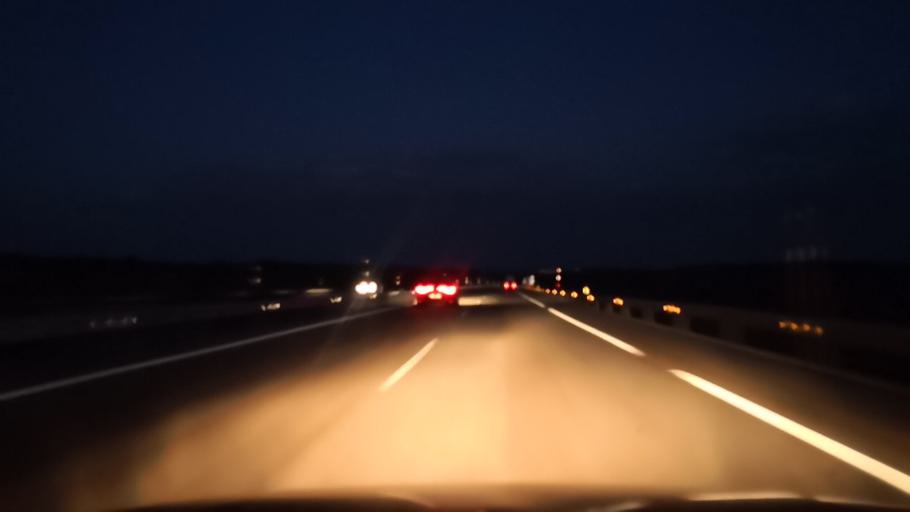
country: ES
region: Castille and Leon
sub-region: Provincia de Leon
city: Brazuelo
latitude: 42.5591
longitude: -6.1929
